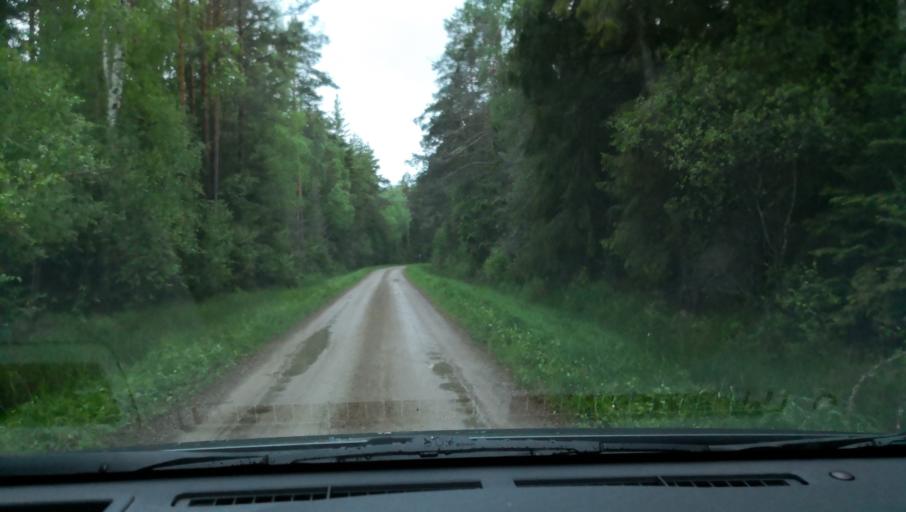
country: SE
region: Uppsala
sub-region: Enkopings Kommun
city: Orsundsbro
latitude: 59.9267
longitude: 17.3346
